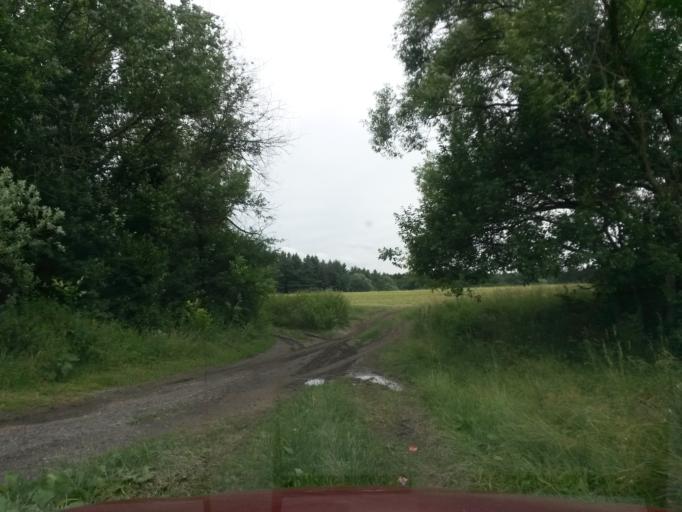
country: SK
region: Nitriansky
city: Handlova
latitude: 48.7405
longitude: 18.7512
